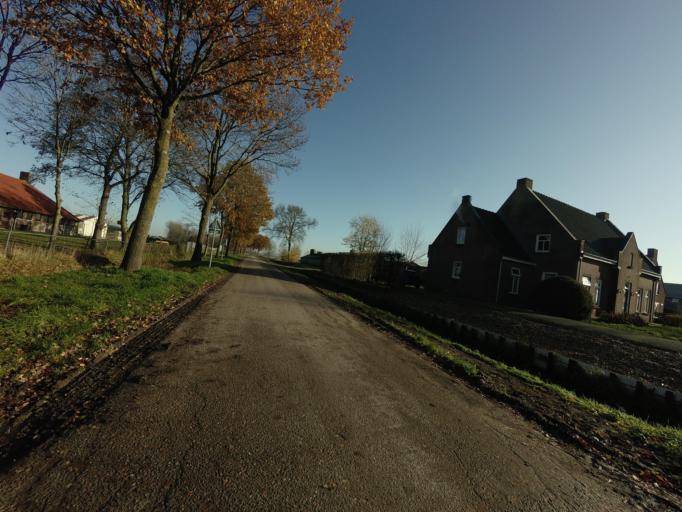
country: NL
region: Gelderland
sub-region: Gemeente Maasdriel
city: Hedel
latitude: 51.7842
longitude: 5.2745
